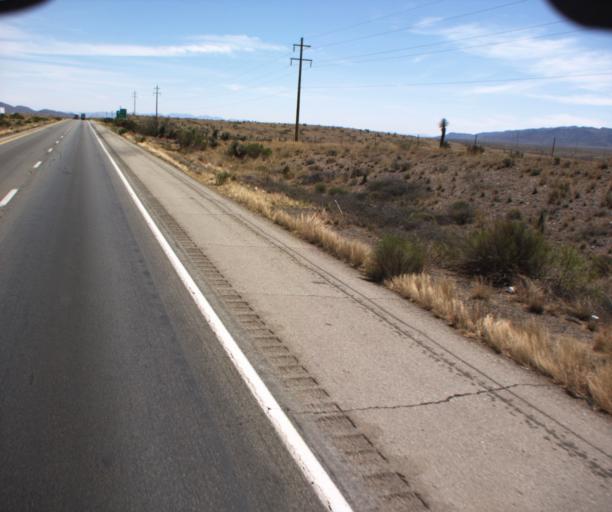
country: US
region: Arizona
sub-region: Cochise County
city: Willcox
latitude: 32.3518
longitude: -109.7242
